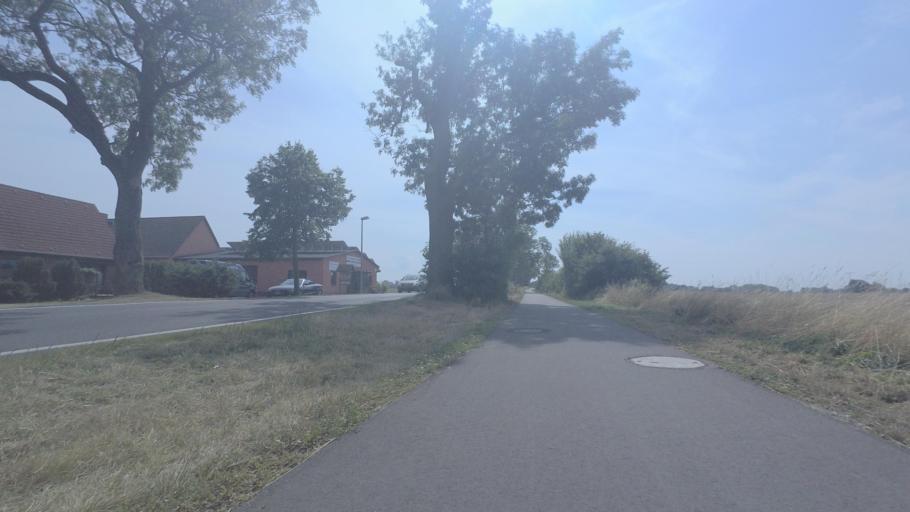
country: DE
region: Mecklenburg-Vorpommern
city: Garz
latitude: 54.2587
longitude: 13.3515
